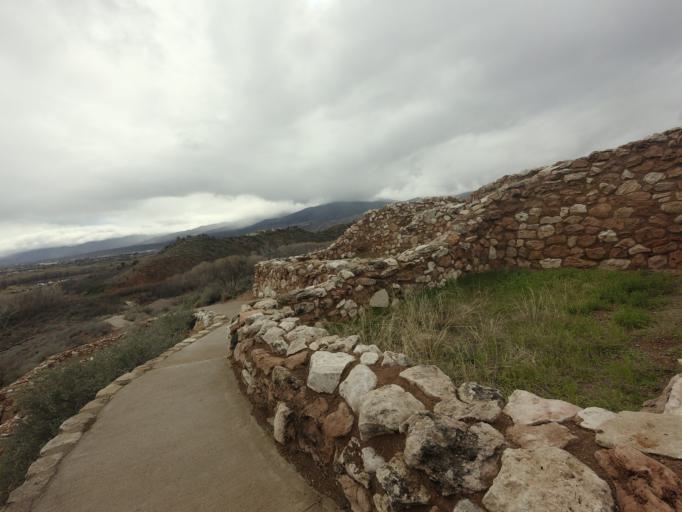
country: US
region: Arizona
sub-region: Yavapai County
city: Clarkdale
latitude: 34.7682
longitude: -112.0268
